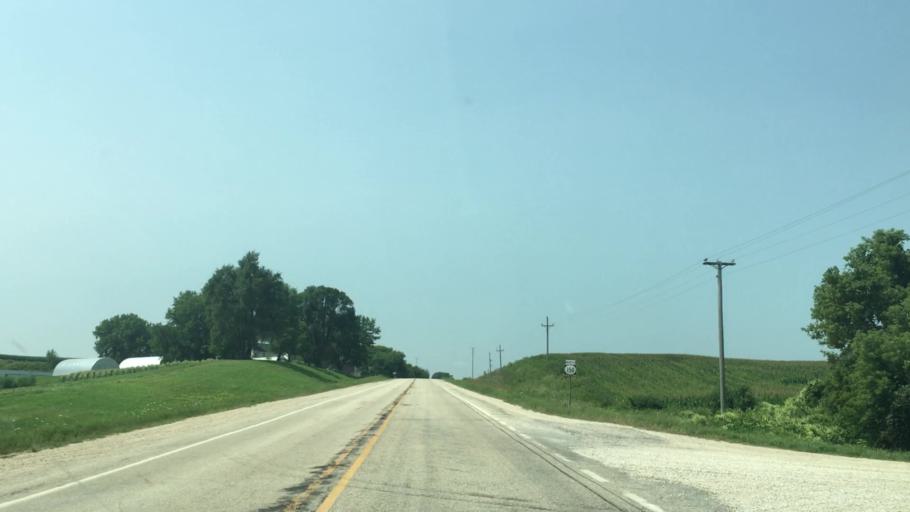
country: US
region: Iowa
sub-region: Fayette County
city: West Union
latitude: 43.0802
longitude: -91.8420
